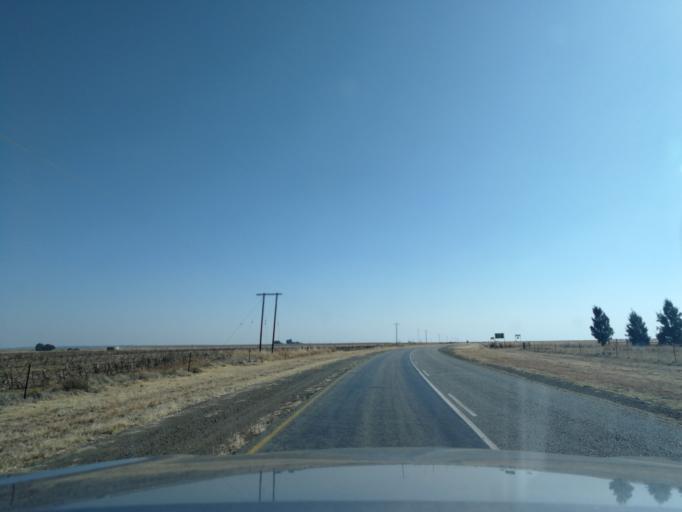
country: ZA
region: Orange Free State
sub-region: Fezile Dabi District Municipality
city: Viljoenskroon
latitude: -27.3932
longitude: 27.0587
